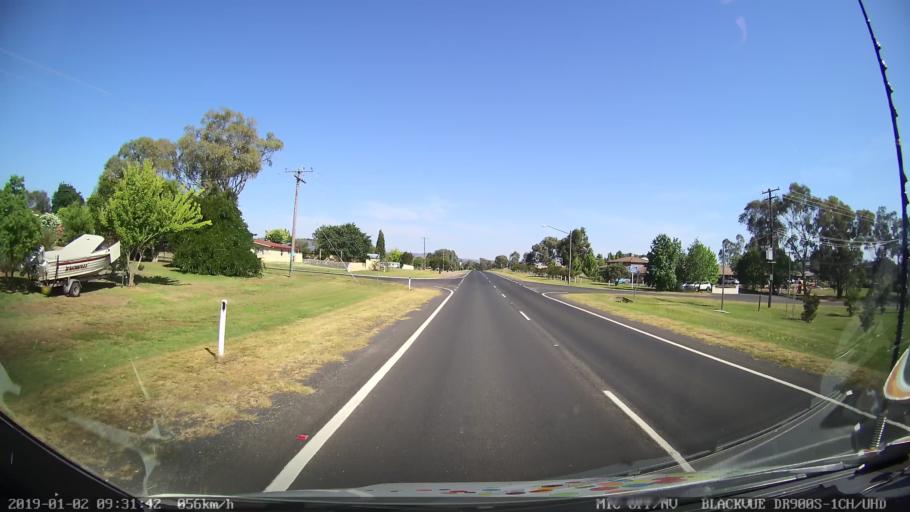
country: AU
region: New South Wales
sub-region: Tumut Shire
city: Tumut
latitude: -35.3169
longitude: 148.2340
